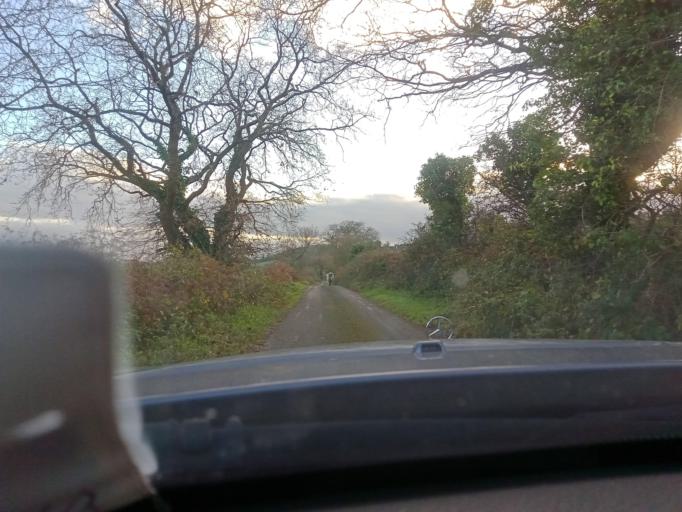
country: IE
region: Leinster
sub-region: Kilkenny
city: Graiguenamanagh
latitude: 52.4972
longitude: -6.9440
